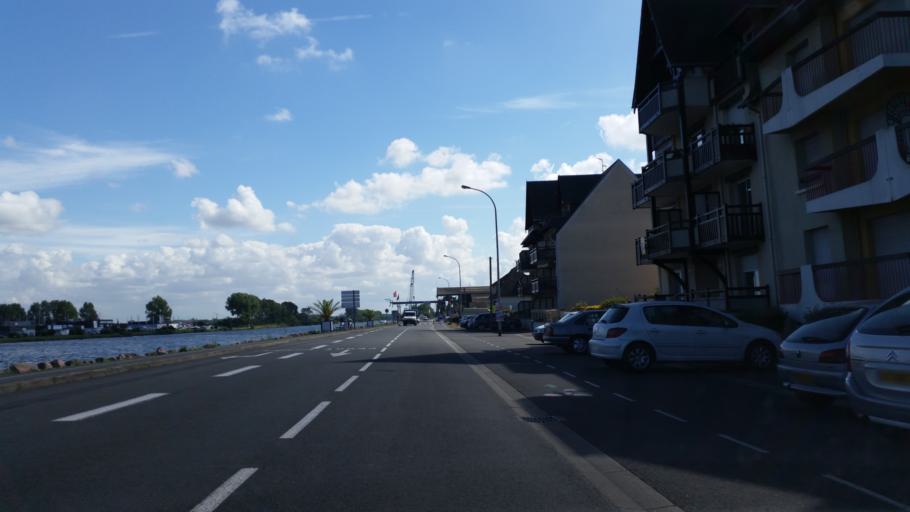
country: FR
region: Lower Normandy
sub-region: Departement du Calvados
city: Ouistreham
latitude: 49.2768
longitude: -0.2507
